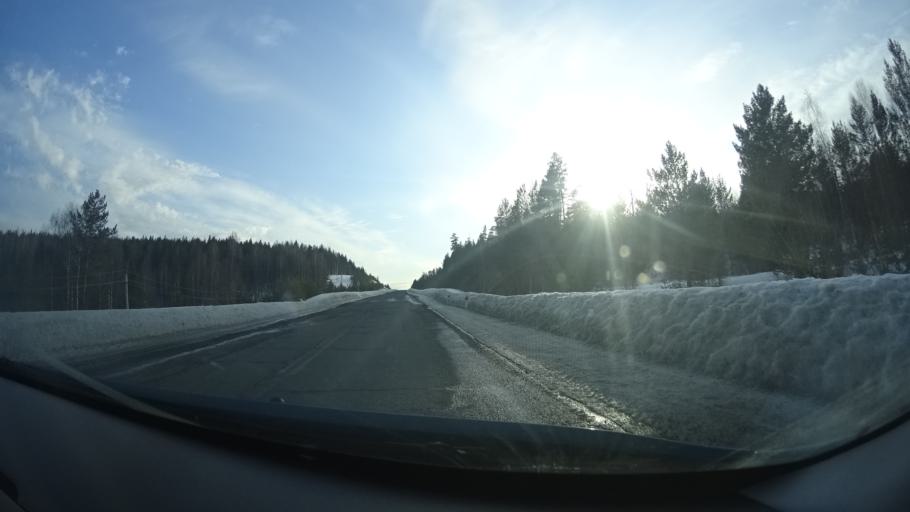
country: RU
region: Bashkortostan
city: Lomovka
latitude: 53.6518
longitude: 58.2083
